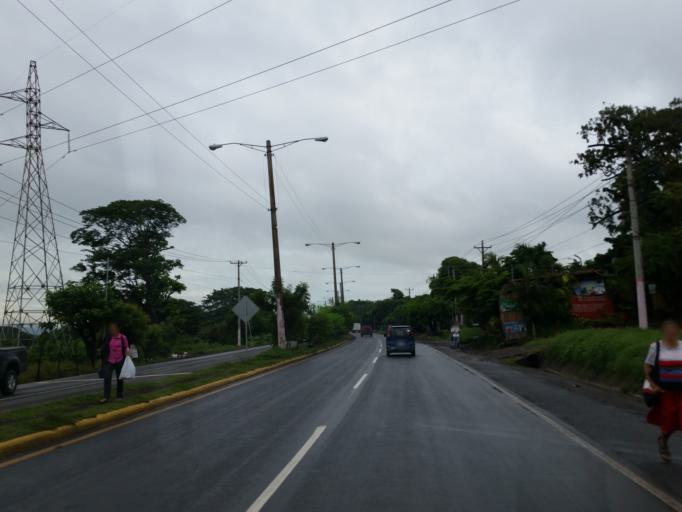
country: NI
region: Managua
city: Ciudad Sandino
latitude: 12.1704
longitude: -86.3437
